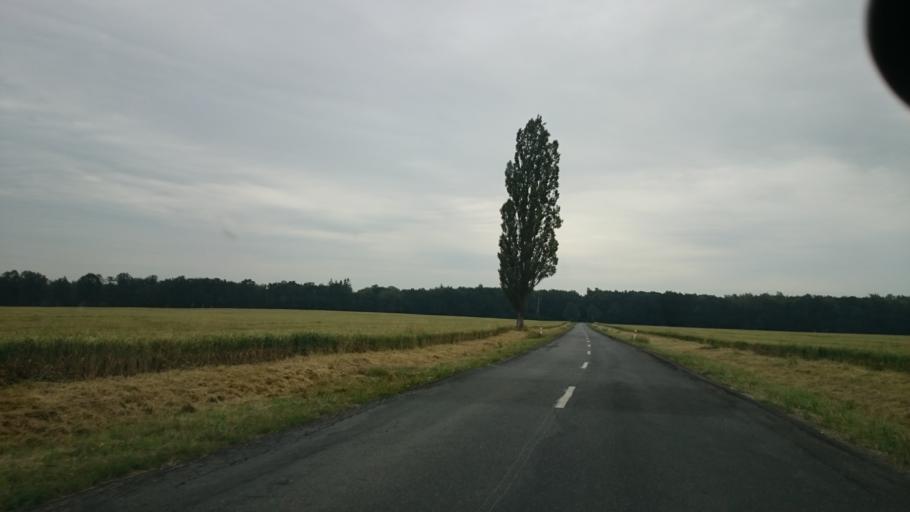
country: PL
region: Lower Silesian Voivodeship
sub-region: Powiat strzelinski
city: Przeworno
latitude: 50.6485
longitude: 17.2306
